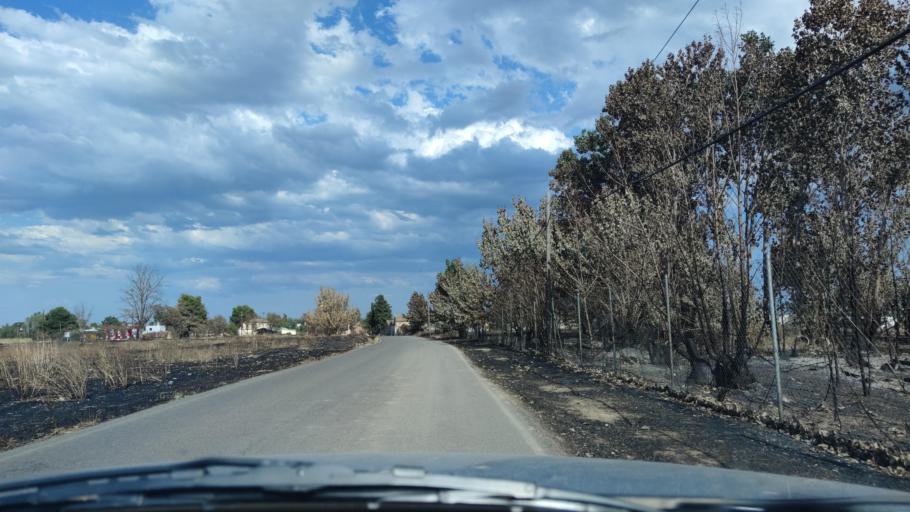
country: ES
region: Catalonia
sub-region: Provincia de Lleida
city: Lleida
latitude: 41.6315
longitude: 0.5888
